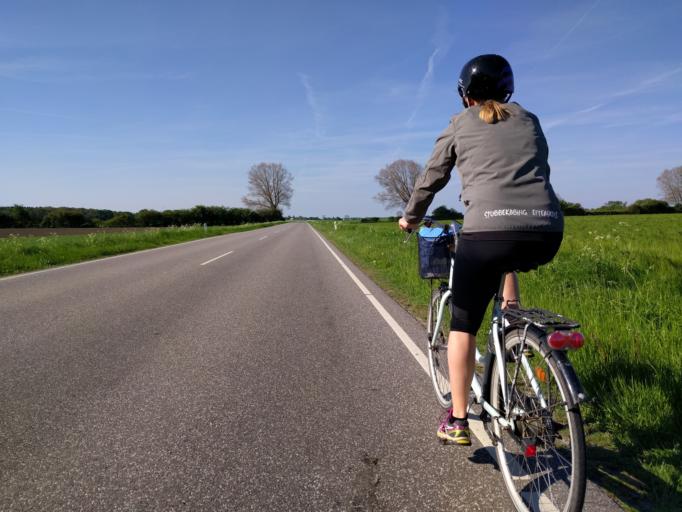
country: DK
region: Zealand
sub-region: Guldborgsund Kommune
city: Stubbekobing
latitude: 54.7898
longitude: 11.9890
